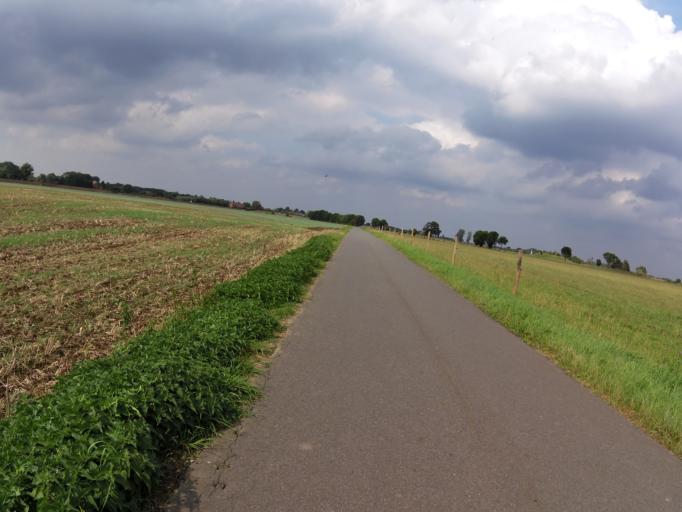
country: DE
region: Lower Saxony
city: Blender
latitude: 52.9038
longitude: 9.1660
